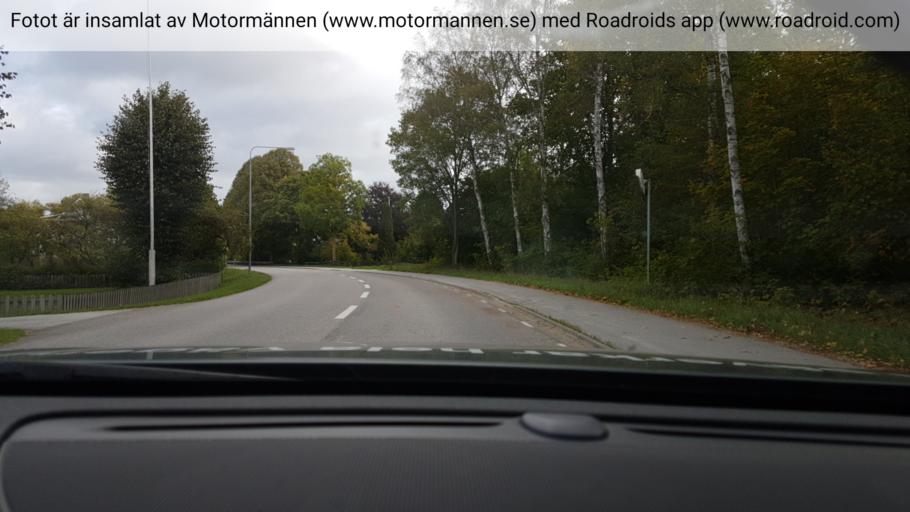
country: SE
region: Gotland
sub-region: Gotland
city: Slite
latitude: 57.7327
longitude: 18.6031
